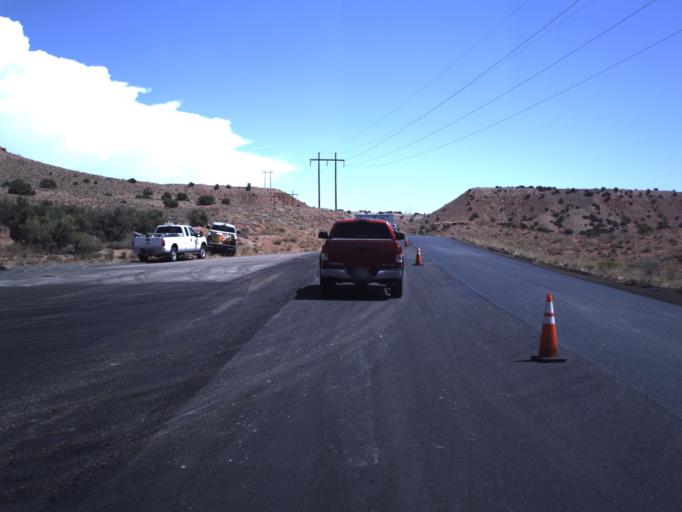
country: US
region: Utah
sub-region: Uintah County
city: Maeser
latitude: 40.4186
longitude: -109.6753
